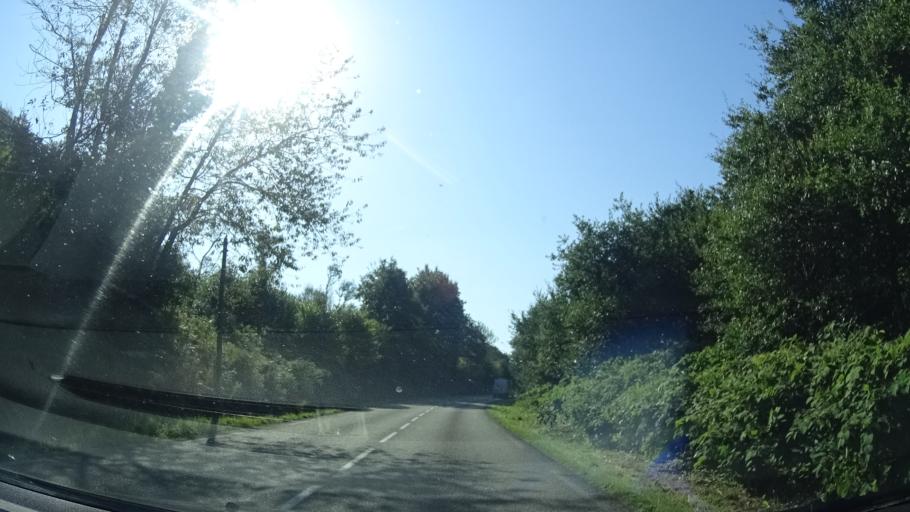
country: FR
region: Brittany
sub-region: Departement du Finistere
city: Chateaulin
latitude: 48.1888
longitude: -4.1095
